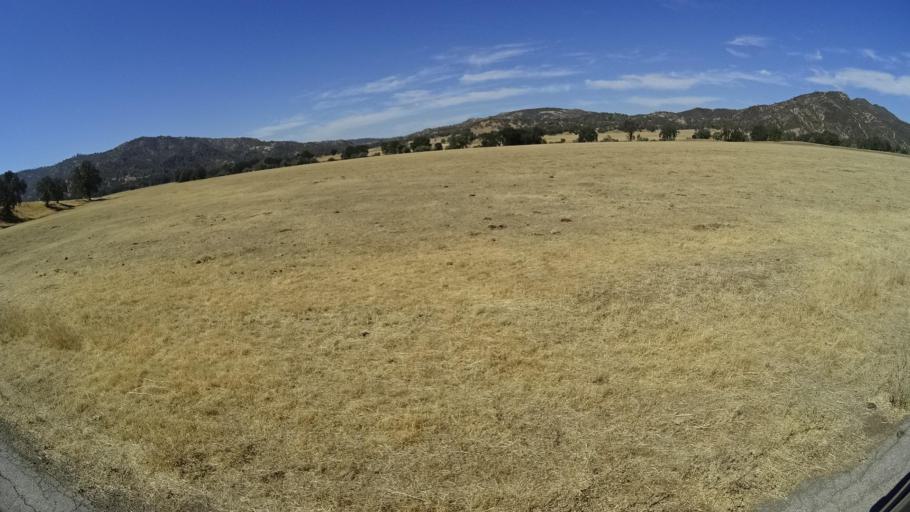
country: US
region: California
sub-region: Fresno County
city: Coalinga
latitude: 36.2066
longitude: -120.6978
